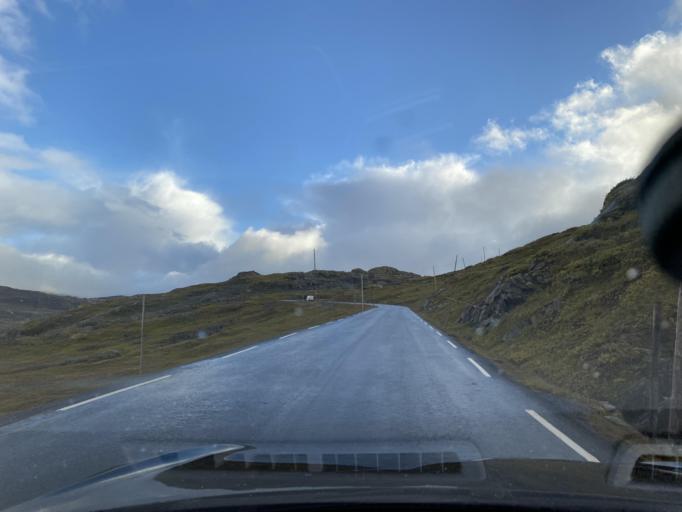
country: NO
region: Sogn og Fjordane
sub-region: Ardal
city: Farnes
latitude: 61.5735
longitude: 8.0313
